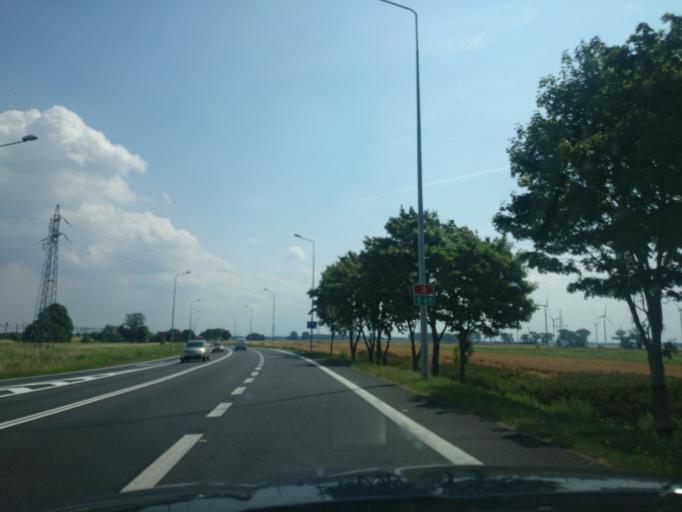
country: PL
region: West Pomeranian Voivodeship
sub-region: Powiat kamienski
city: Wolin
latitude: 53.8443
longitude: 14.6322
